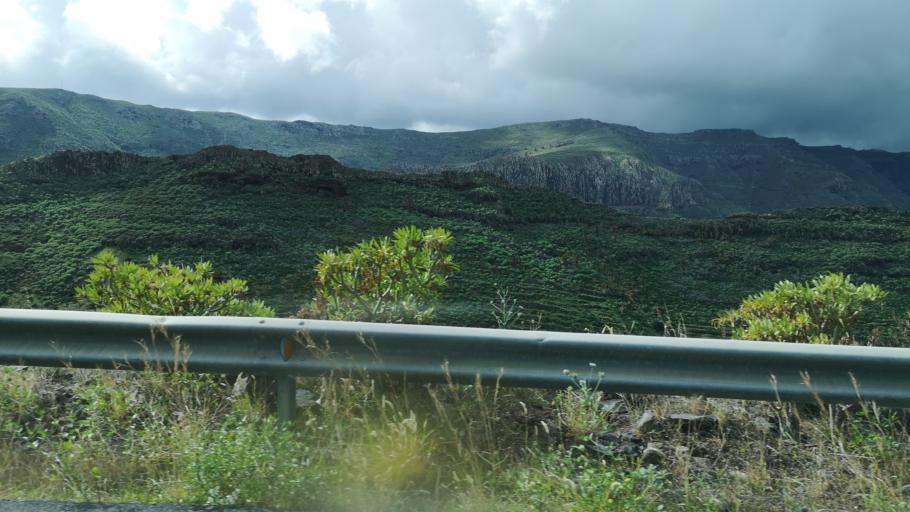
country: ES
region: Canary Islands
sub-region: Provincia de Santa Cruz de Tenerife
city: San Sebastian de la Gomera
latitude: 28.1122
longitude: -17.1329
